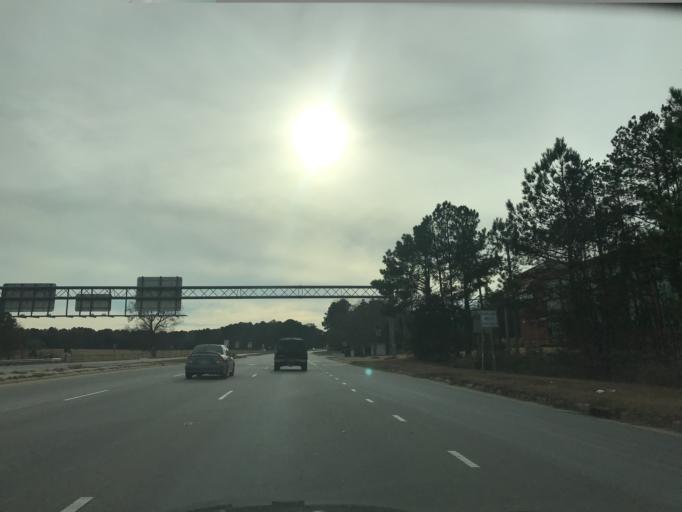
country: US
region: North Carolina
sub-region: Wake County
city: Knightdale
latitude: 35.8612
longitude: -78.5496
